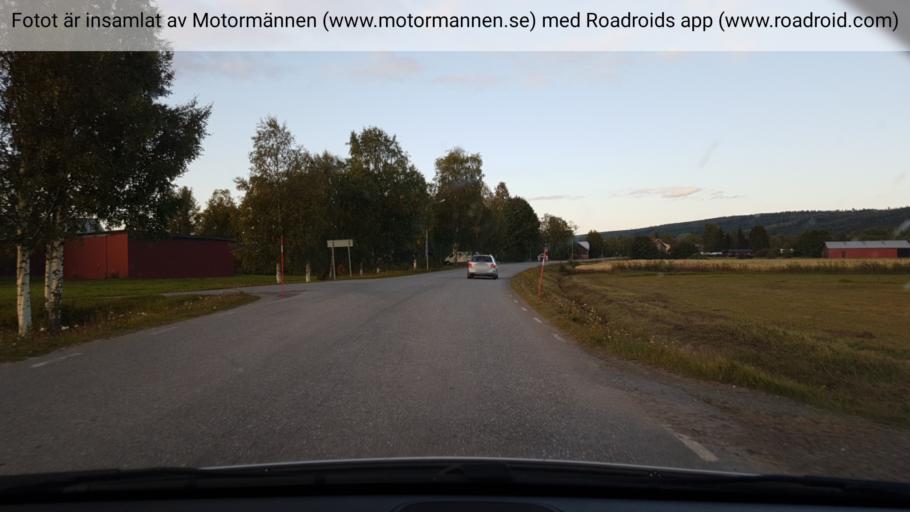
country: SE
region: Vaesterbotten
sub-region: Vannas Kommun
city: Vannasby
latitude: 63.9359
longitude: 19.8606
